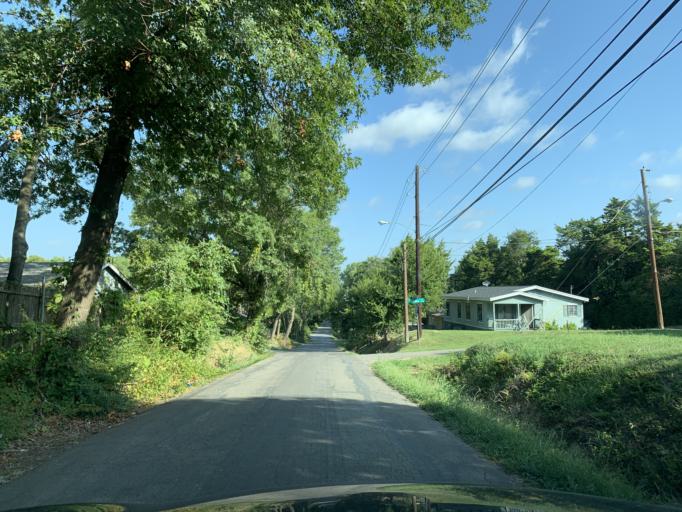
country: US
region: Texas
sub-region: Dallas County
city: Hutchins
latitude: 32.6766
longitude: -96.7775
